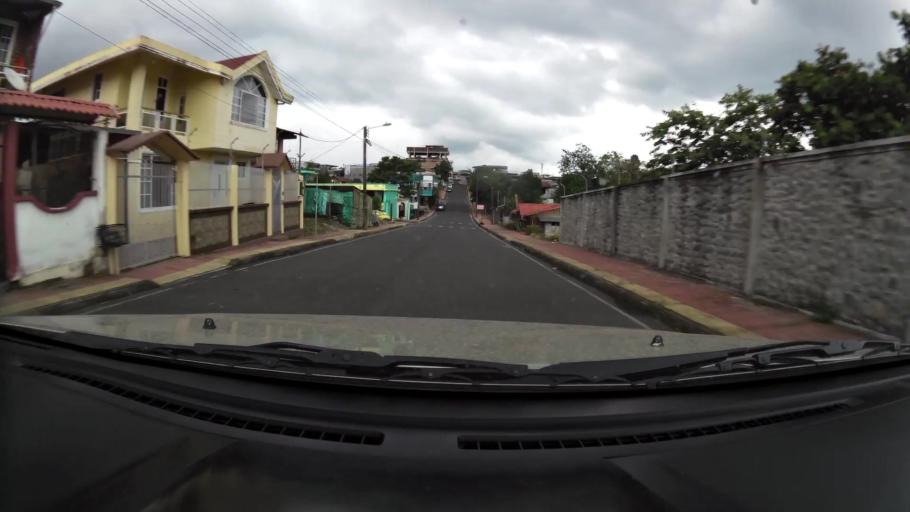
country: EC
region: Pastaza
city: Puyo
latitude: -1.4913
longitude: -77.9983
